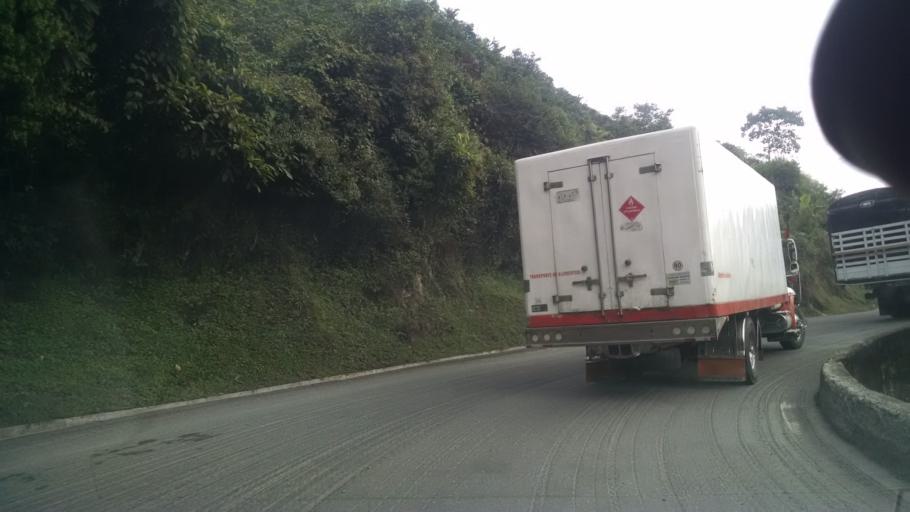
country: CO
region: Antioquia
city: Santa Barbara
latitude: 5.9018
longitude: -75.5748
